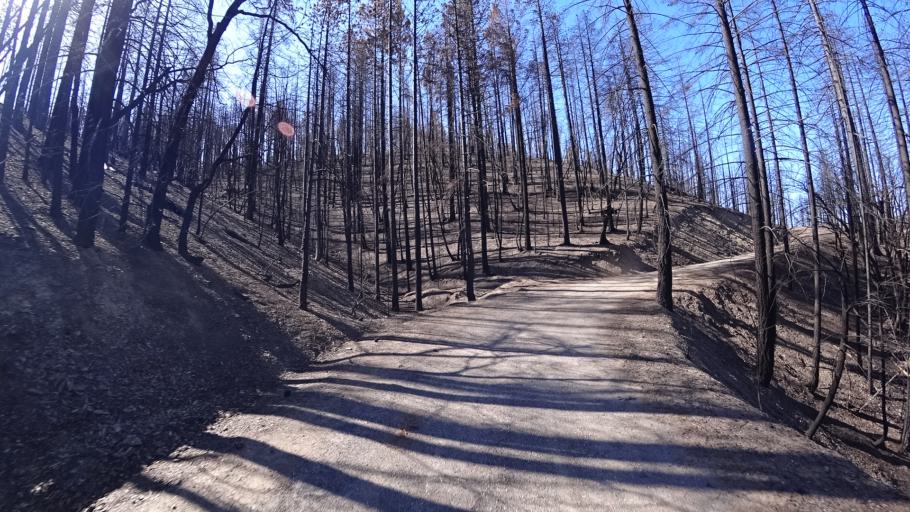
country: US
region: California
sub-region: Tehama County
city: Rancho Tehama Reserve
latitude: 39.6708
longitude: -122.7078
